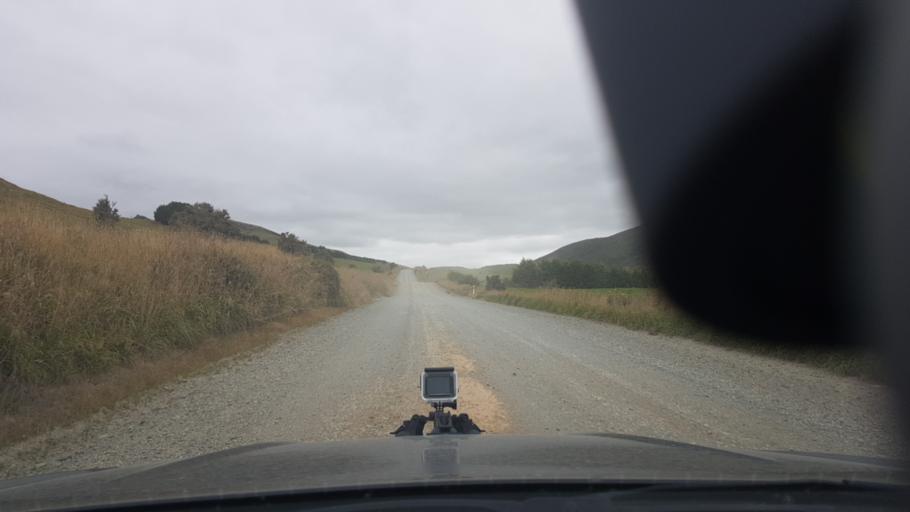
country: NZ
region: Otago
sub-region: Clutha District
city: Papatowai
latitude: -46.3403
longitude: 169.4224
